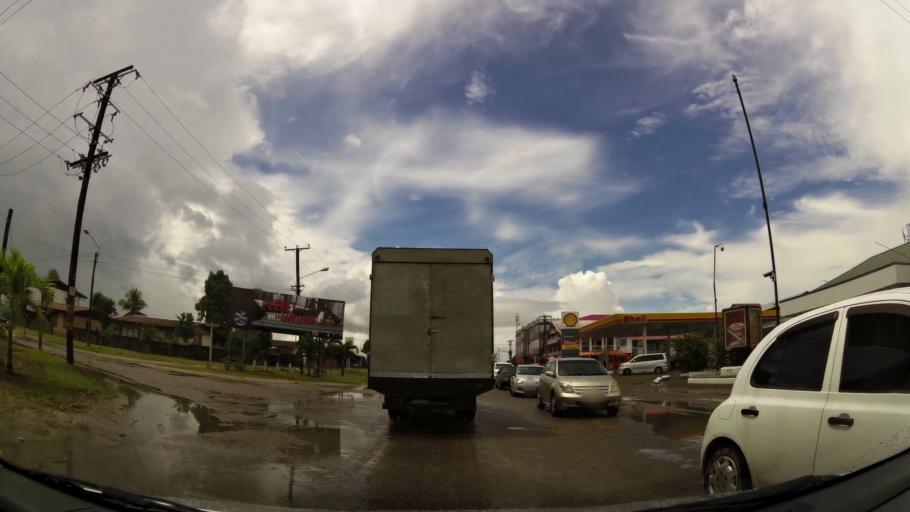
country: SR
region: Paramaribo
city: Paramaribo
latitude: 5.8041
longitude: -55.1883
